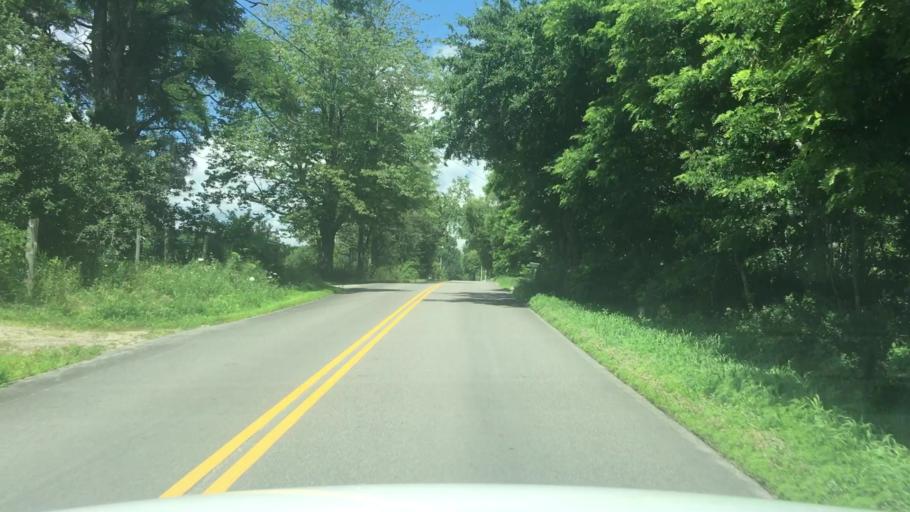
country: US
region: Maine
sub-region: Waldo County
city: Belfast
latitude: 44.4112
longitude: -69.0373
